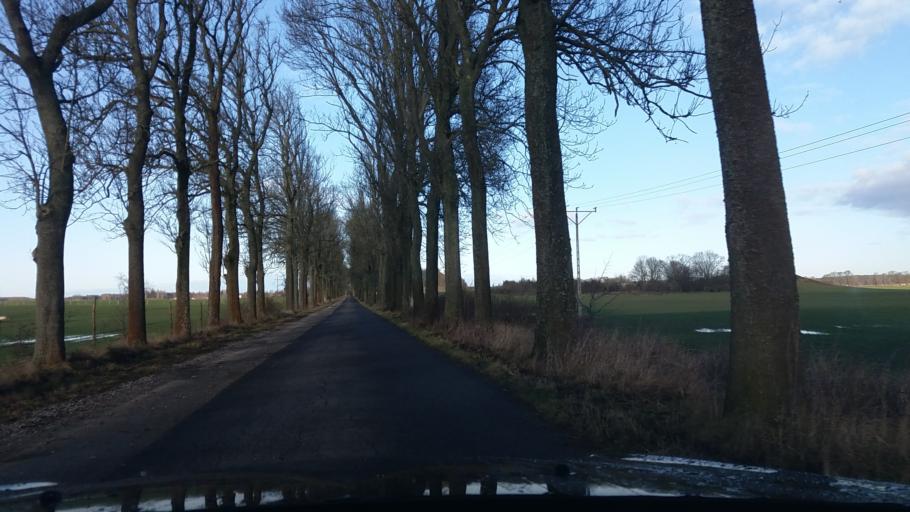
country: PL
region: West Pomeranian Voivodeship
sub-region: Powiat choszczenski
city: Drawno
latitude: 53.2029
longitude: 15.7793
